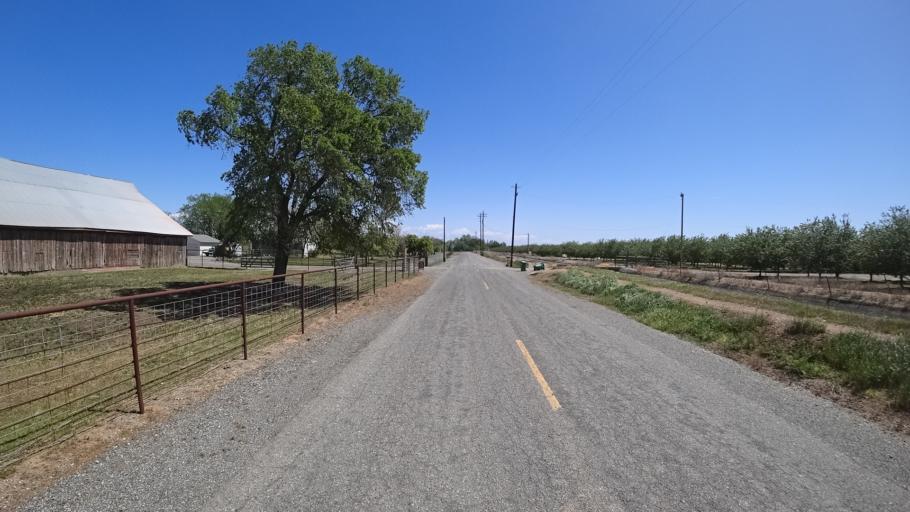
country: US
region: California
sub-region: Glenn County
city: Orland
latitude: 39.7951
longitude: -122.2361
